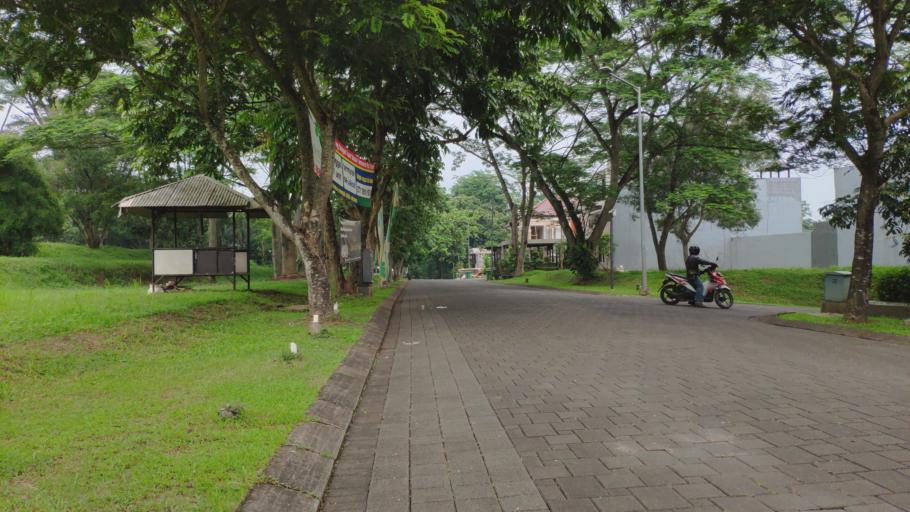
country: ID
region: West Java
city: Depok
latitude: -6.3546
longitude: 106.7955
